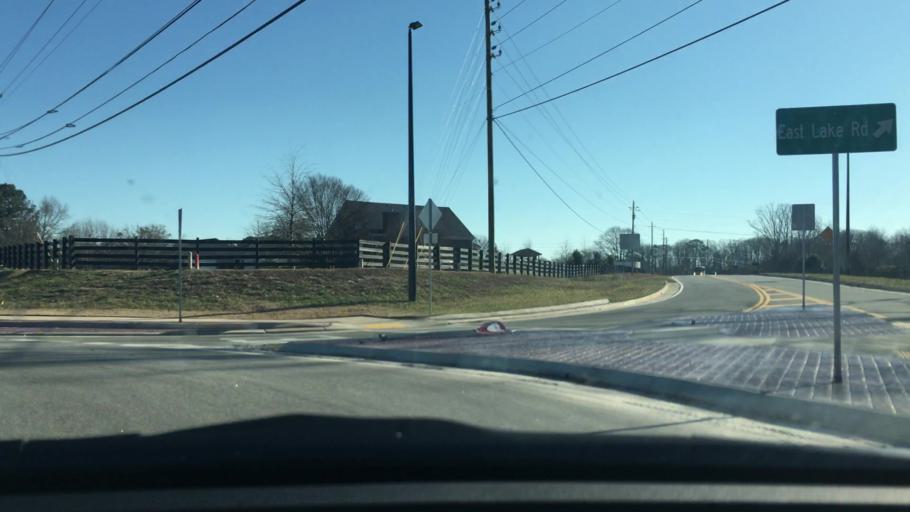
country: US
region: Georgia
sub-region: Henry County
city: McDonough
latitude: 33.5014
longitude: -84.0785
